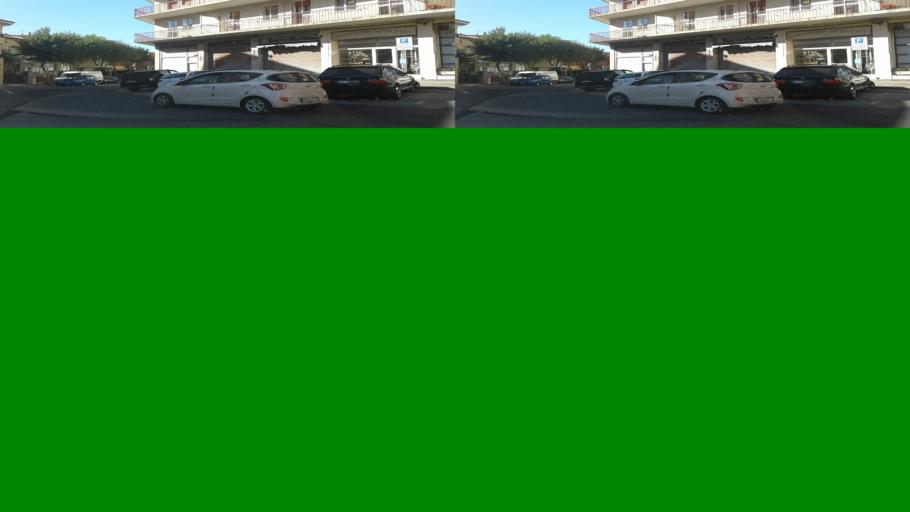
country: IT
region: Sardinia
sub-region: Provincia di Olbia-Tempio
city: Tempio Pausania
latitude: 40.9014
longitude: 9.1016
